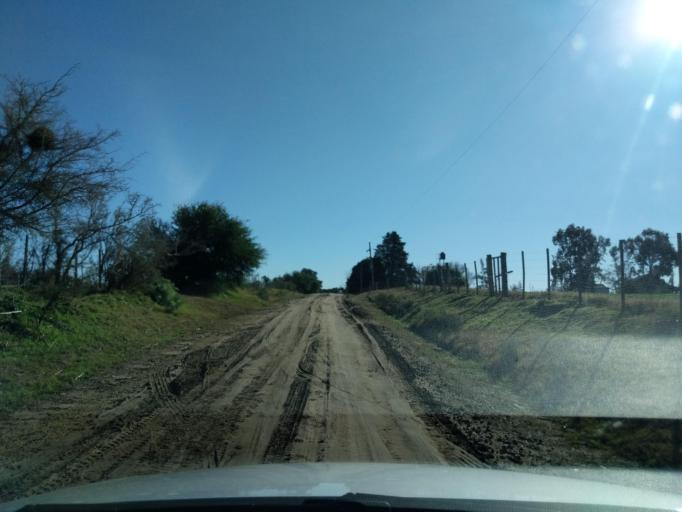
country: UY
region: Florida
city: Florida
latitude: -34.0719
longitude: -56.2676
